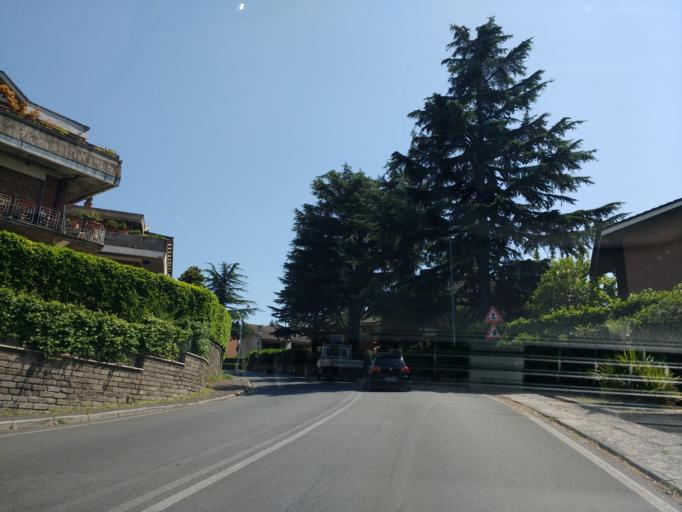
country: IT
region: Latium
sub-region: Citta metropolitana di Roma Capitale
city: Grottaferrata
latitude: 41.7817
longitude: 12.6838
